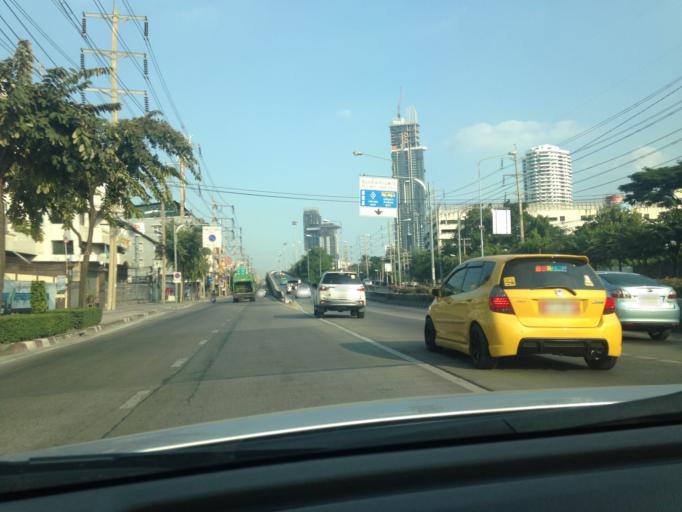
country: TH
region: Bangkok
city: Bang Kho Laem
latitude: 13.6900
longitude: 100.5058
